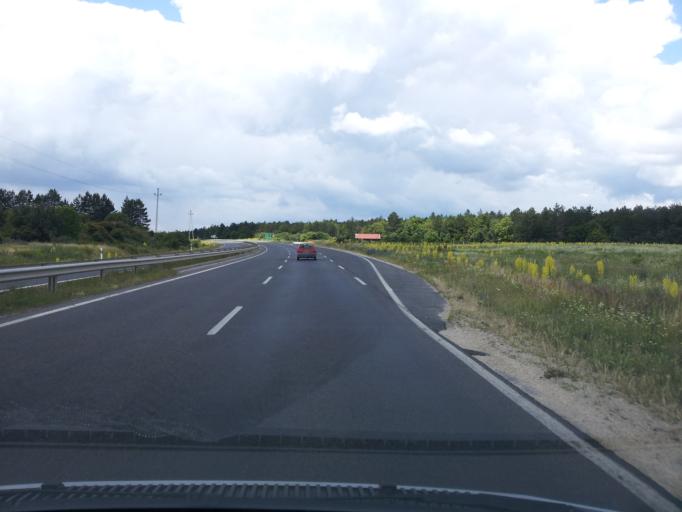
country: HU
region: Veszprem
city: Nemesvamos
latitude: 47.1180
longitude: 17.8412
